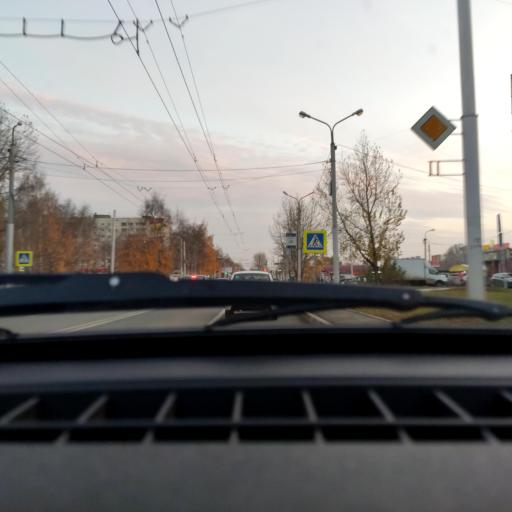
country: RU
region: Bashkortostan
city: Ufa
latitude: 54.7814
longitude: 56.1243
